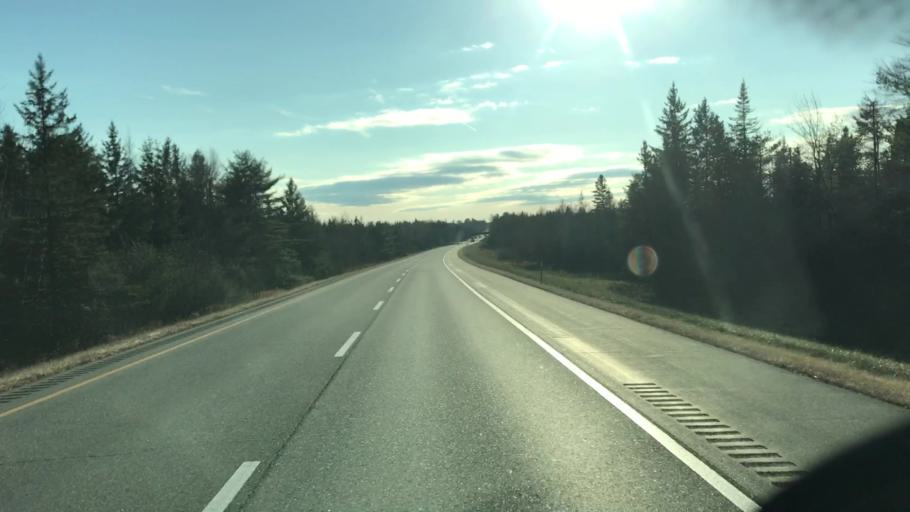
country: US
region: Maine
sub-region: Waldo County
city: Burnham
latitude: 44.7110
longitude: -69.4506
